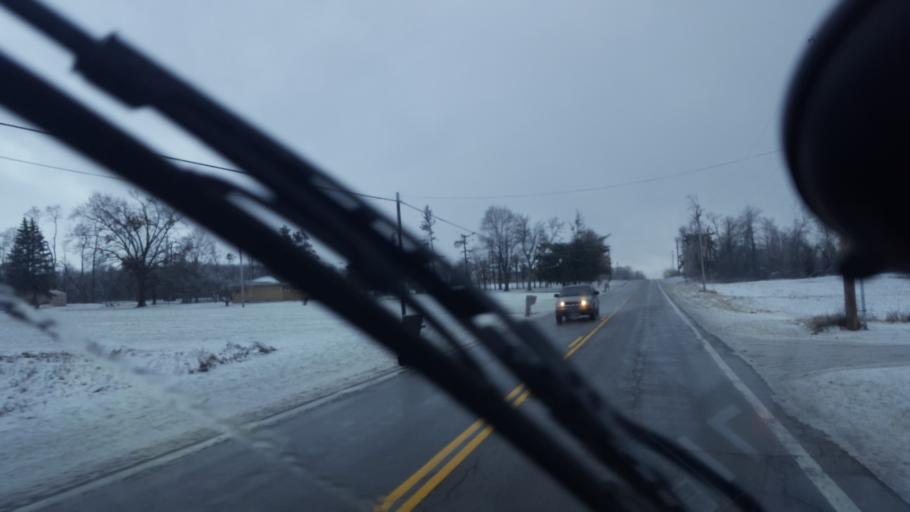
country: US
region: Ohio
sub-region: Richland County
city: Lexington
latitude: 40.6505
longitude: -82.5902
